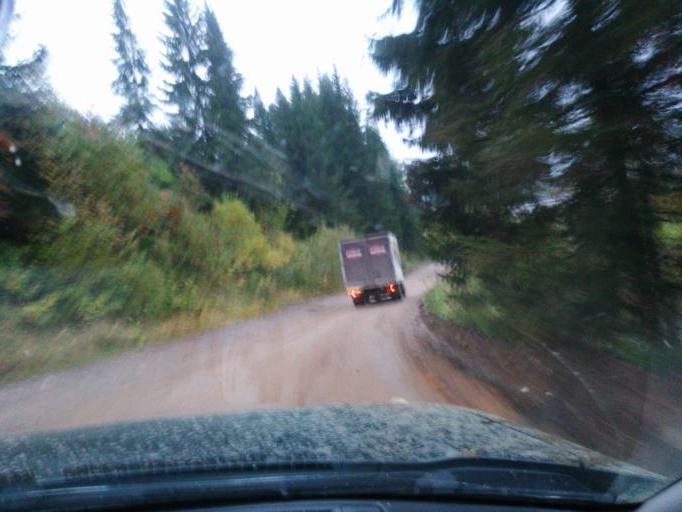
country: RU
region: Sverdlovsk
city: Sylva
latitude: 57.7978
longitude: 58.5342
